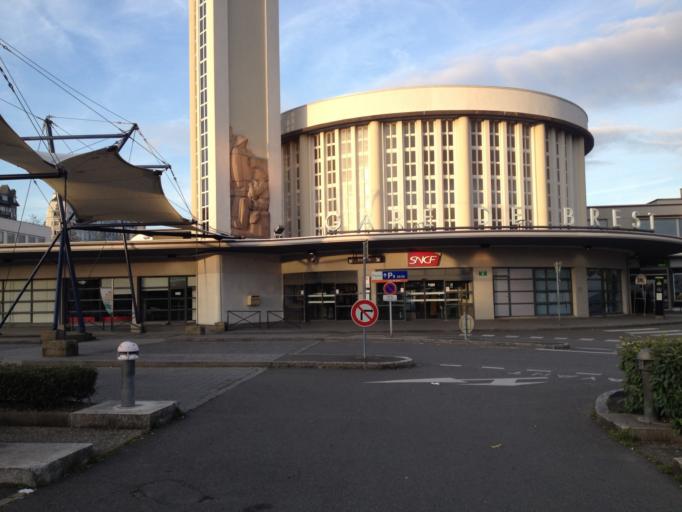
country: FR
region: Brittany
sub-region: Departement du Finistere
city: Brest
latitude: 48.3876
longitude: -4.4808
